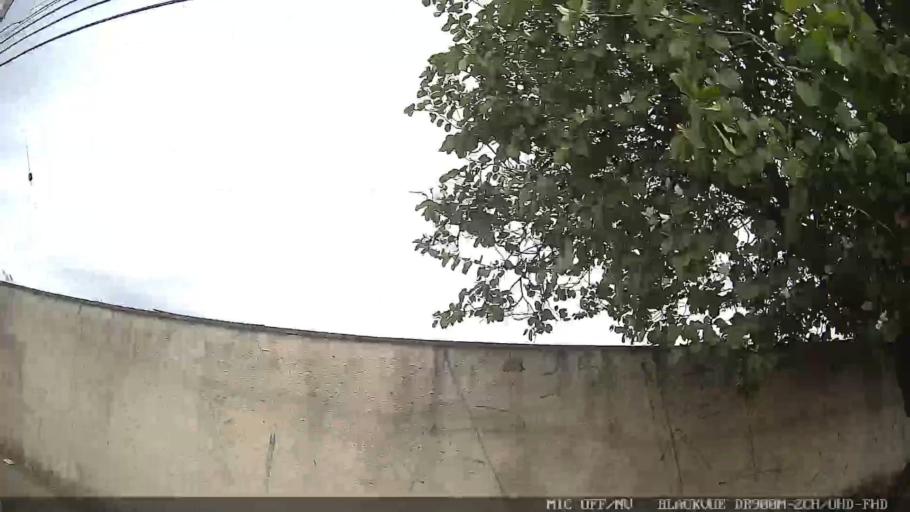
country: BR
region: Sao Paulo
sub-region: Salto
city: Salto
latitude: -23.1914
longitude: -47.2797
